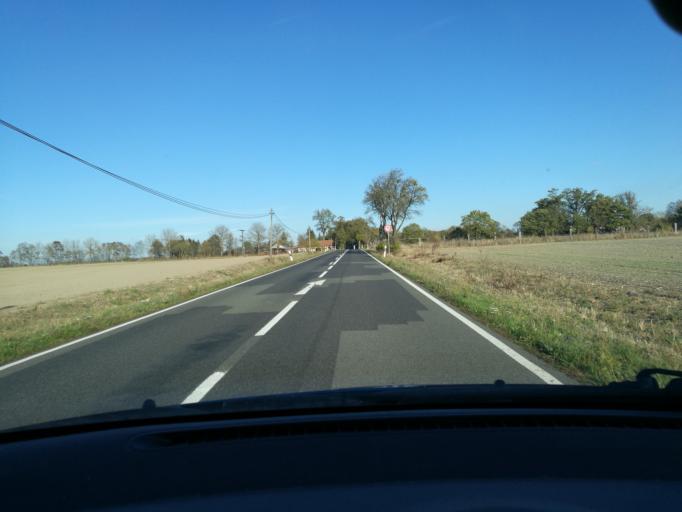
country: DE
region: Brandenburg
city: Lanz
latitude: 53.1474
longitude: 11.5750
